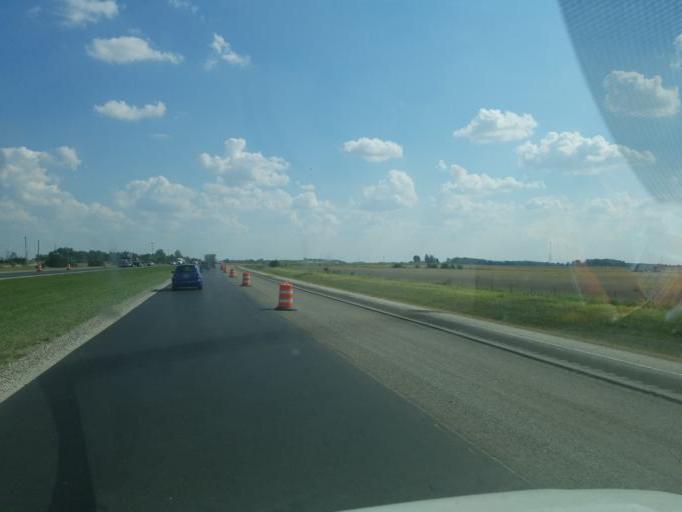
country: US
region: Ohio
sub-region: Van Wert County
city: Convoy
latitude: 40.9491
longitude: -84.7200
